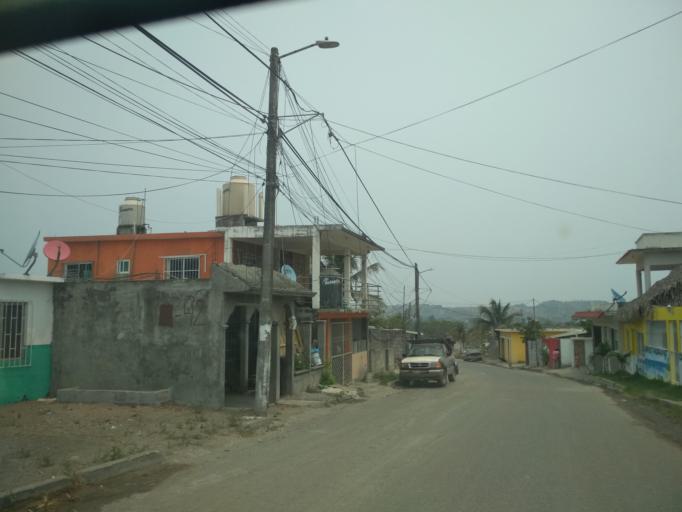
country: MX
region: Veracruz
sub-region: Veracruz
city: Fraccionamiento Costa Dorada
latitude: 19.2099
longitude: -96.2144
